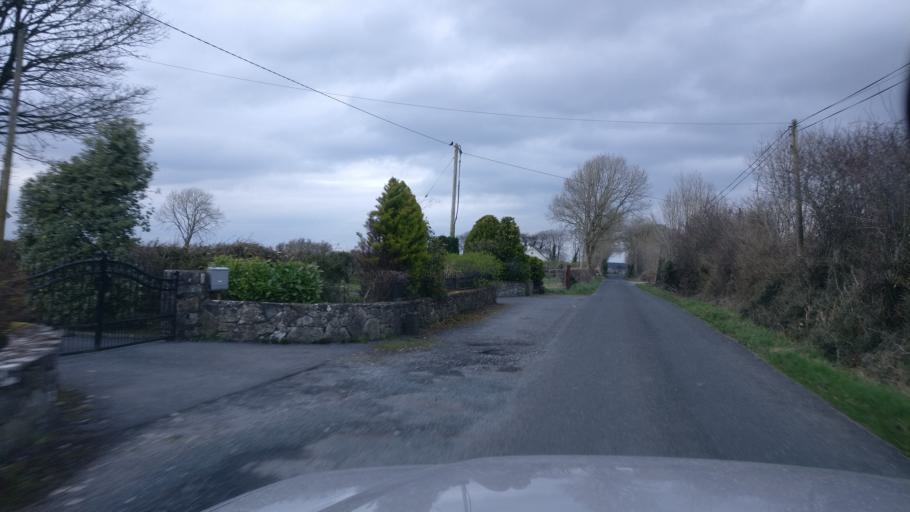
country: IE
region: Connaught
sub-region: County Galway
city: Loughrea
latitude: 53.2522
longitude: -8.5118
